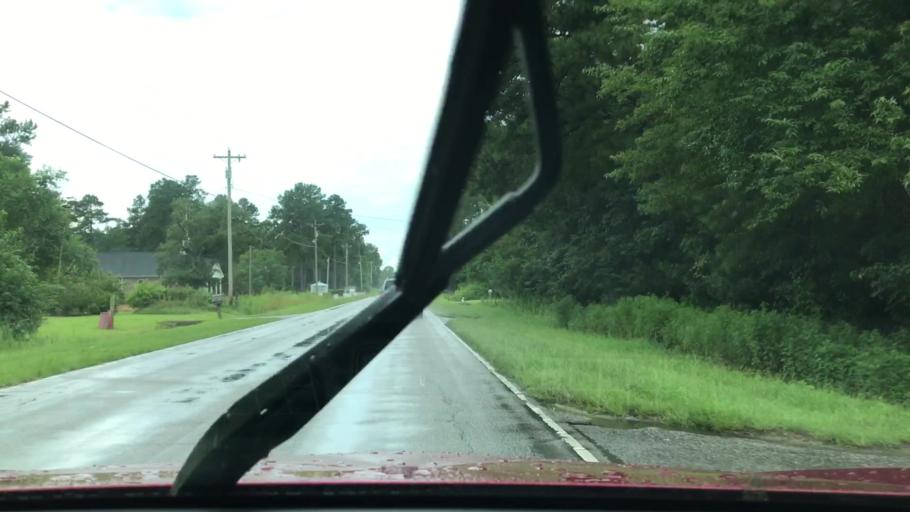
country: US
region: South Carolina
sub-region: Horry County
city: Red Hill
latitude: 33.8553
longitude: -79.0071
